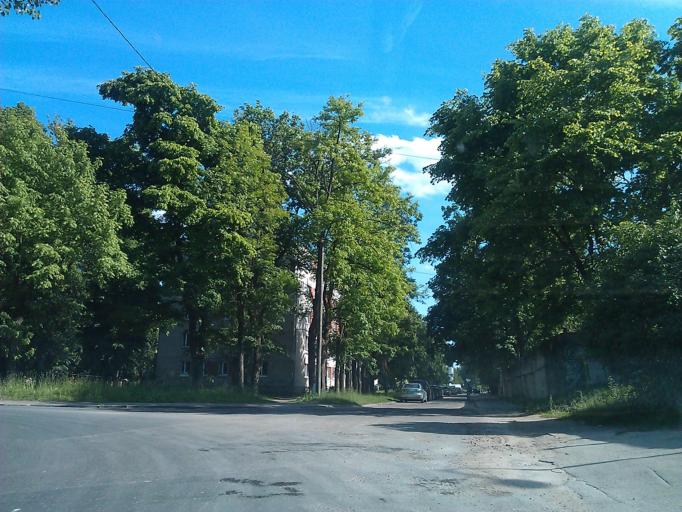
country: LV
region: Riga
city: Jaunciems
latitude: 56.9934
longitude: 24.2280
